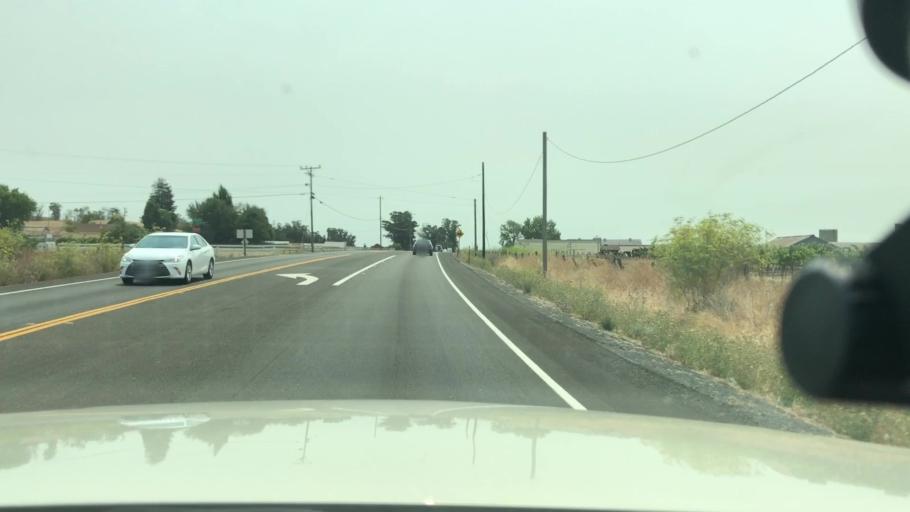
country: US
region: California
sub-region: Marin County
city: Black Point-Green Point
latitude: 38.1592
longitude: -122.5007
